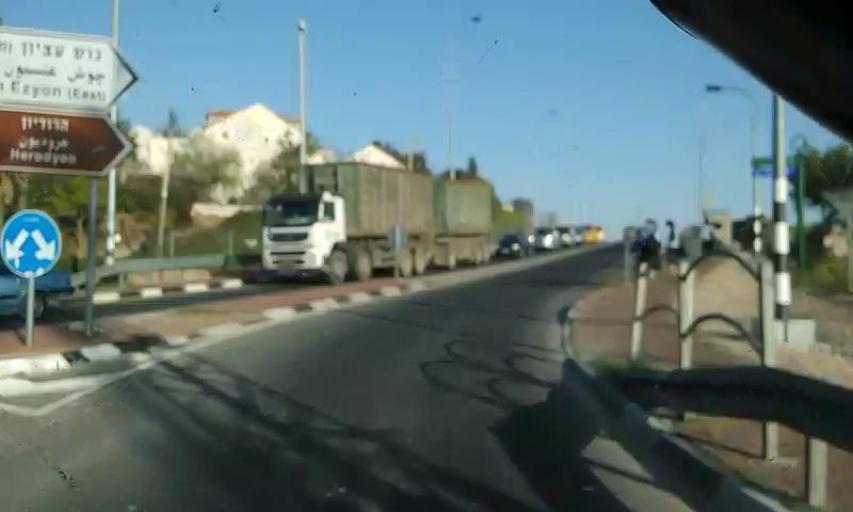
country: PS
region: West Bank
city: Jurat ash Sham`ah
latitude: 31.6482
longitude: 35.1473
